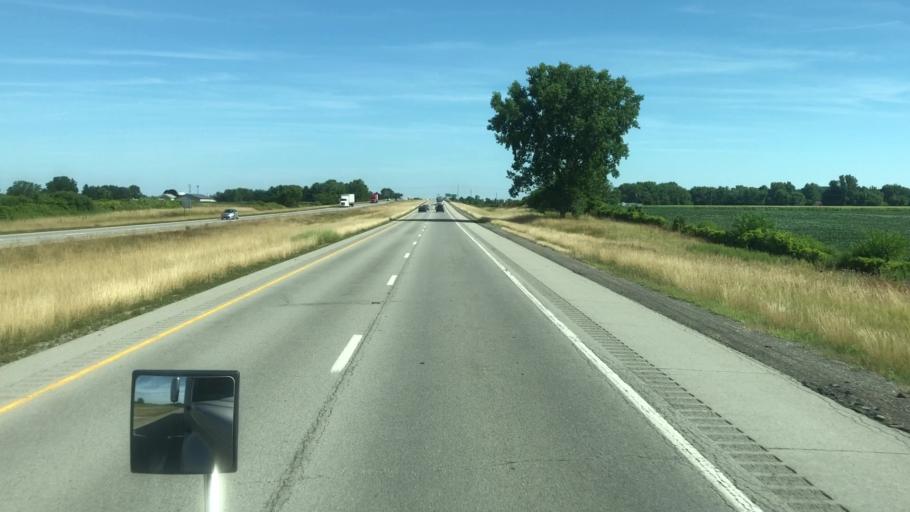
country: US
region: Ohio
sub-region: Erie County
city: Huron
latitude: 41.3838
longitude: -82.5737
